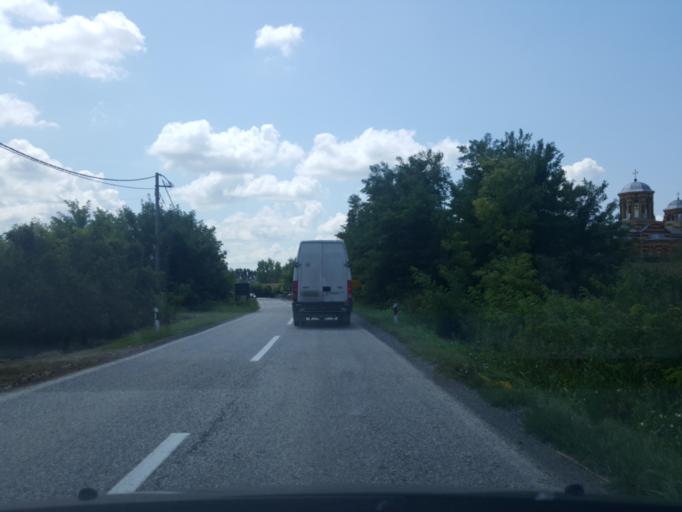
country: RS
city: Glusci
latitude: 44.8992
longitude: 19.5448
